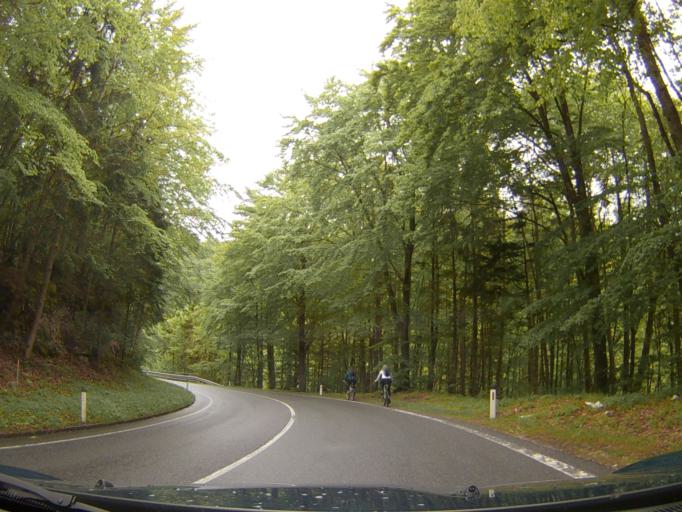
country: AT
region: Upper Austria
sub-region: Politischer Bezirk Vocklabruck
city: Sankt Lorenz
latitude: 47.7928
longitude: 13.3925
